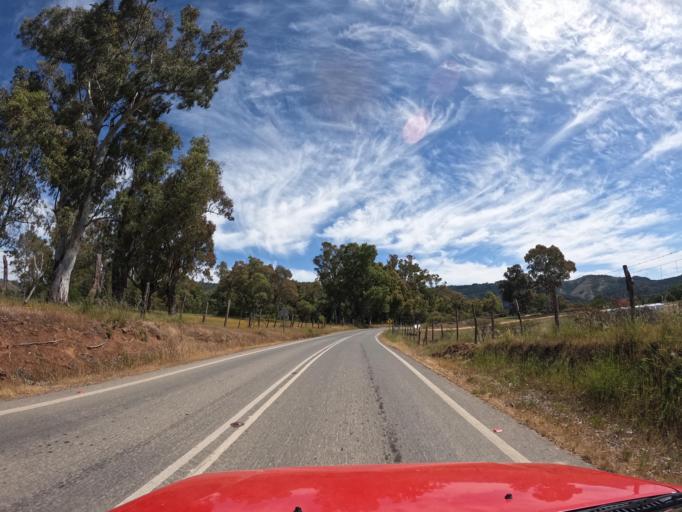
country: CL
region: Maule
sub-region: Provincia de Talca
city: Talca
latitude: -35.0023
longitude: -71.7954
